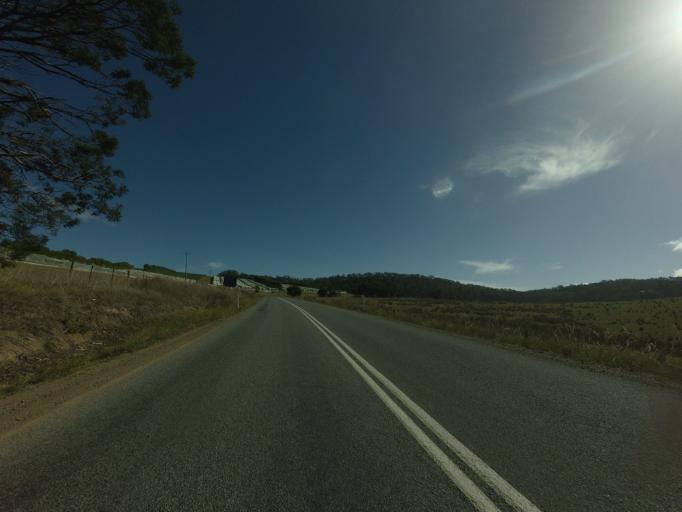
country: AU
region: Tasmania
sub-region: Break O'Day
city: St Helens
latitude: -41.9623
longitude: 148.1574
